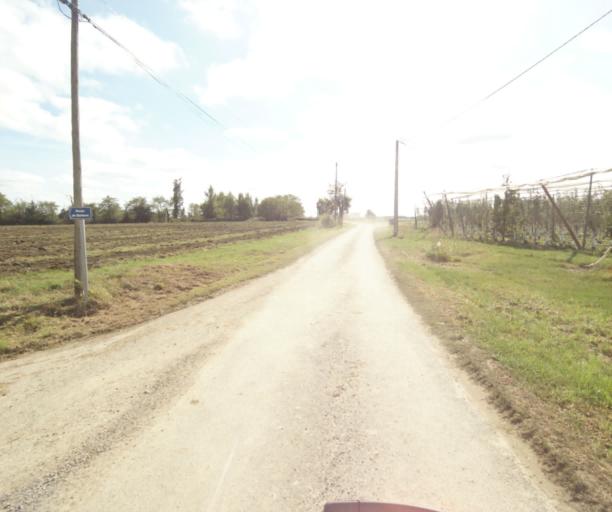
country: FR
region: Midi-Pyrenees
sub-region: Departement du Tarn-et-Garonne
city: Montech
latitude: 43.9408
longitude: 1.2065
